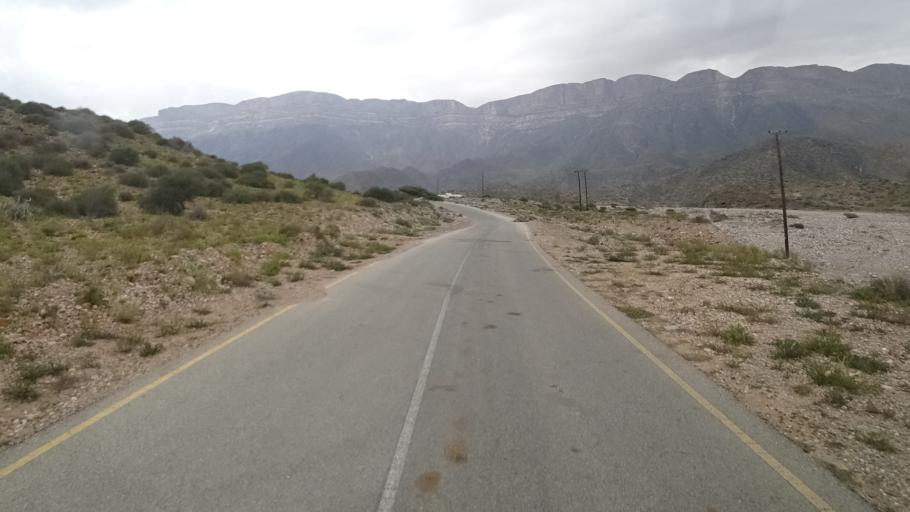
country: OM
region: Zufar
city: Salalah
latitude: 17.1714
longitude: 54.9721
